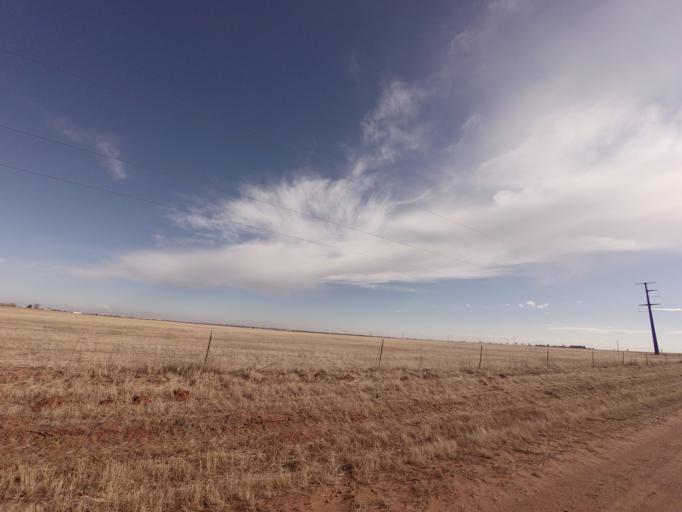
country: US
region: New Mexico
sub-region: Curry County
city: Texico
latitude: 34.4022
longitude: -103.1258
